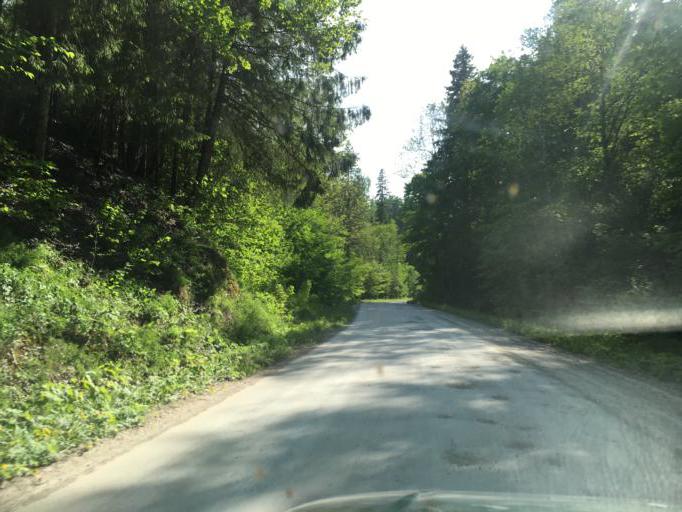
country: LV
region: Dundaga
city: Dundaga
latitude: 57.6100
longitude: 22.4769
